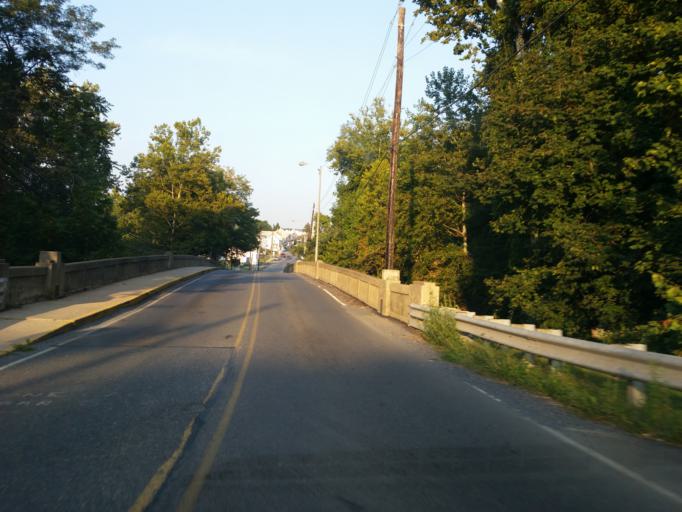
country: US
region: Pennsylvania
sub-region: Lebanon County
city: Jonestown
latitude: 40.4125
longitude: -76.4878
